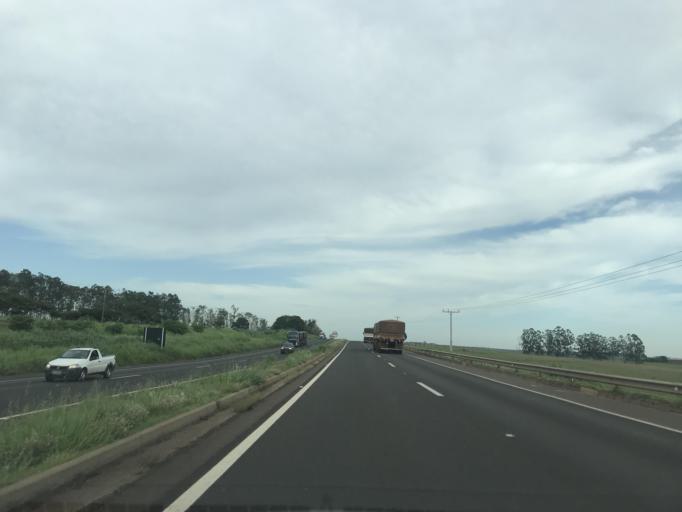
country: BR
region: Parana
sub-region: Alto Parana
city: Alto Parana
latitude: -23.1195
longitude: -52.3171
